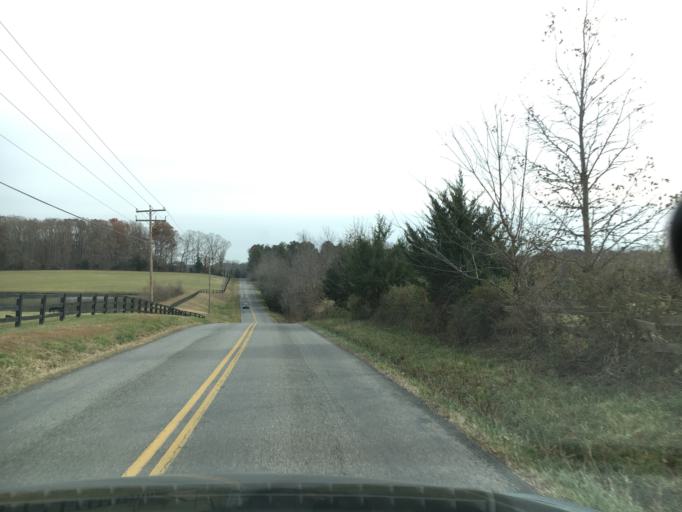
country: US
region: Virginia
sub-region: Henrico County
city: Wyndham
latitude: 37.6817
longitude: -77.6808
